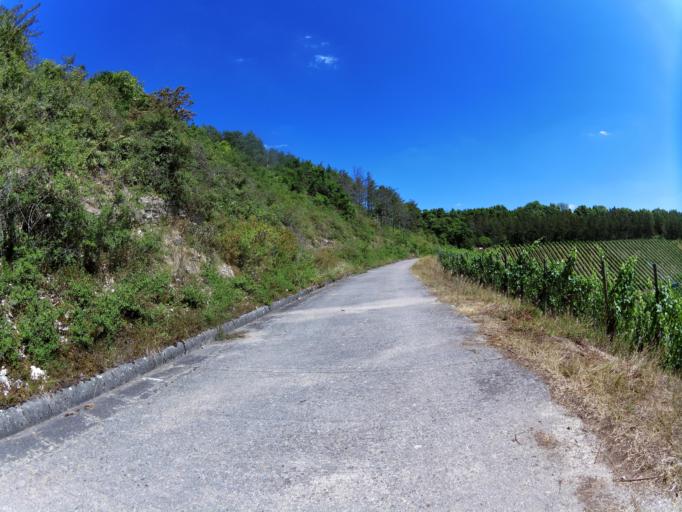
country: DE
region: Bavaria
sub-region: Regierungsbezirk Unterfranken
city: Thungersheim
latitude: 49.8918
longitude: 9.8533
